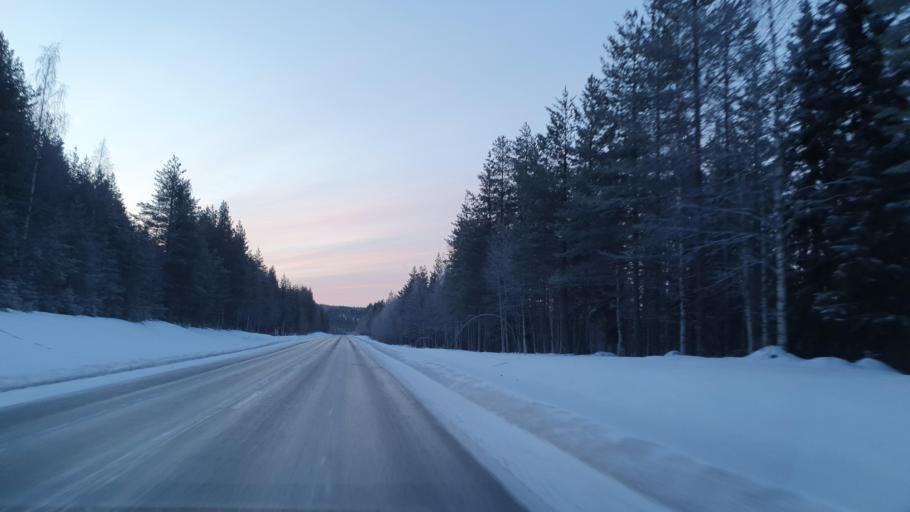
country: FI
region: Lapland
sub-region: Torniolaakso
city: Pello
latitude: 66.9936
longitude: 24.0463
